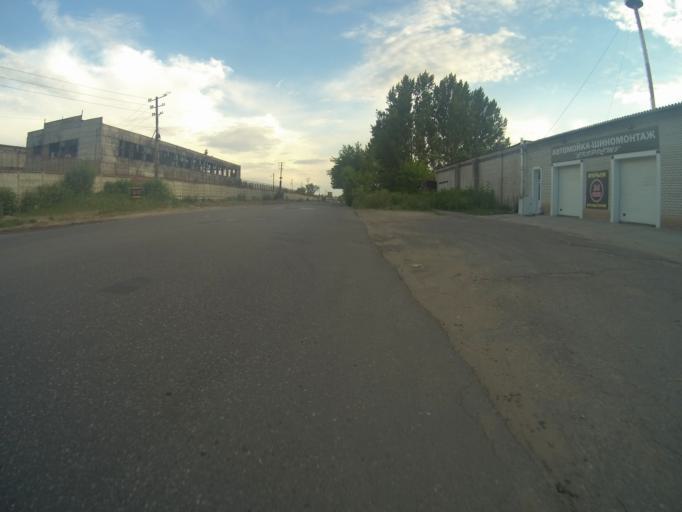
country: RU
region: Vladimir
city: Vladimir
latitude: 56.1593
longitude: 40.3860
